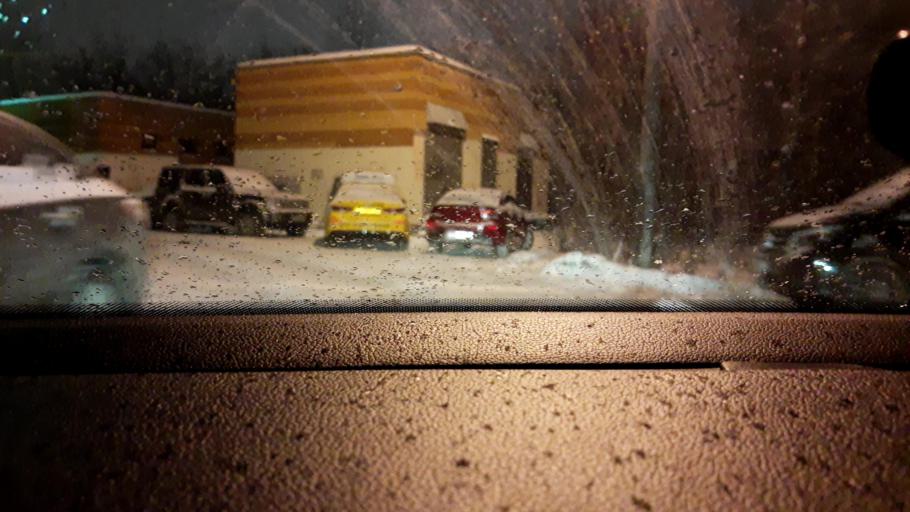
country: RU
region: Moscow
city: Yaroslavskiy
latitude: 55.8967
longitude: 37.7096
